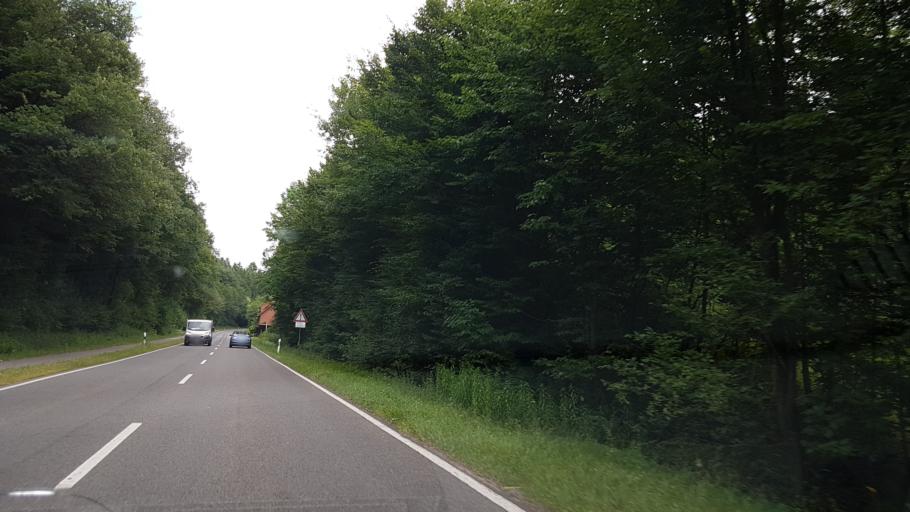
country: DE
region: Saarland
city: Quierschied
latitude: 49.2957
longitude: 7.0170
